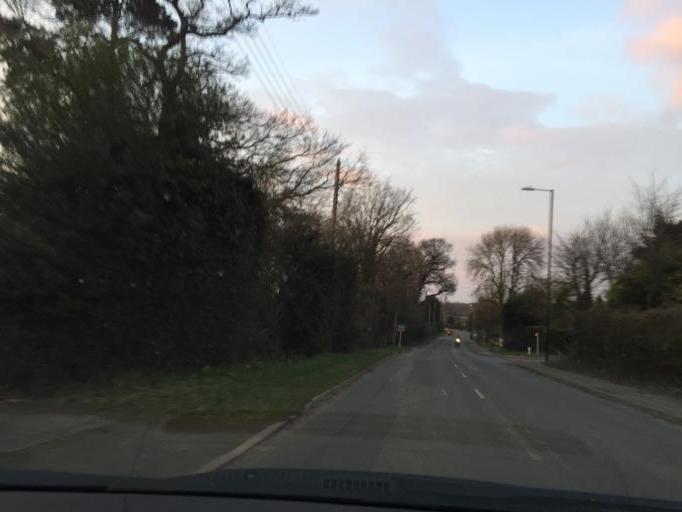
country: GB
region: England
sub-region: Warwickshire
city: Kenilworth
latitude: 52.3900
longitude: -1.5985
